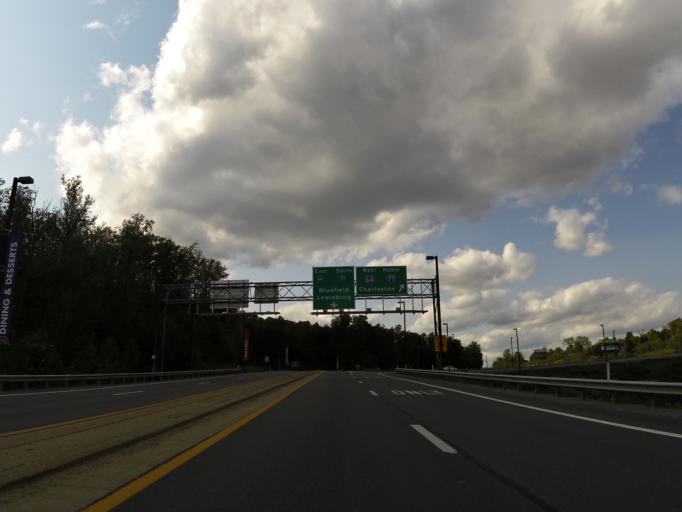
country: US
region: West Virginia
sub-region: Raleigh County
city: Prosperity
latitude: 37.8086
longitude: -81.2138
